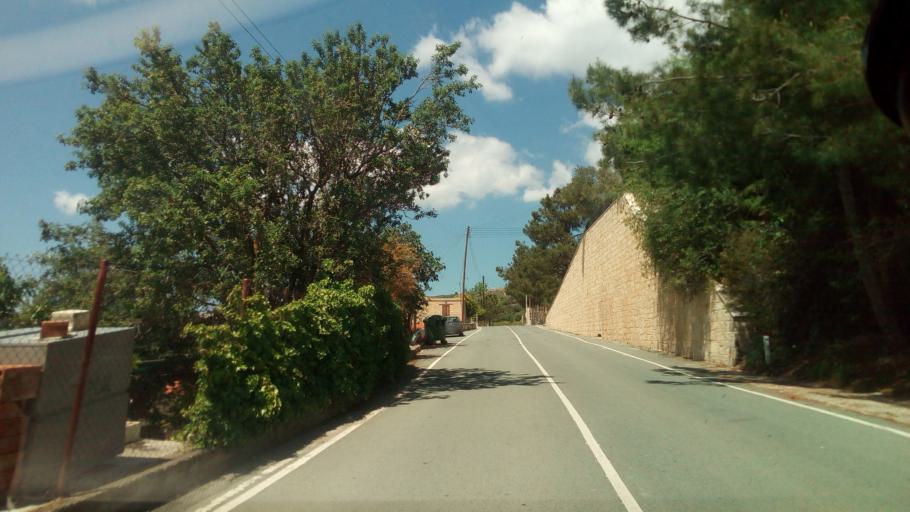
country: CY
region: Limassol
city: Pachna
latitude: 34.8415
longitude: 32.7708
